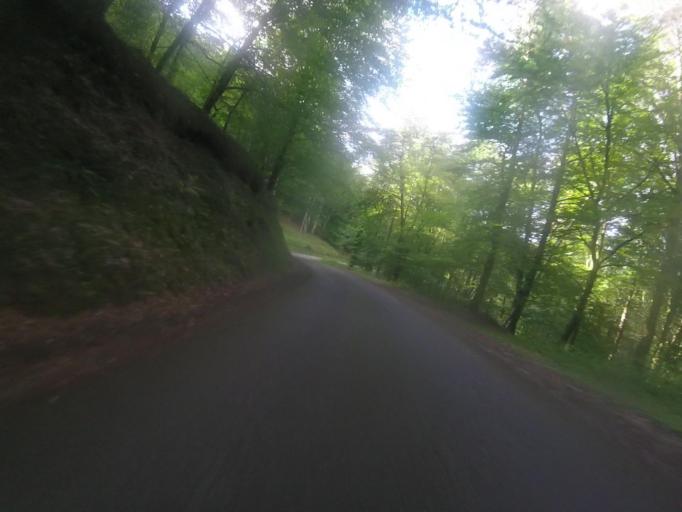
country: ES
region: Navarre
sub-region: Provincia de Navarra
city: Goizueta
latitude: 43.2339
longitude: -1.8055
